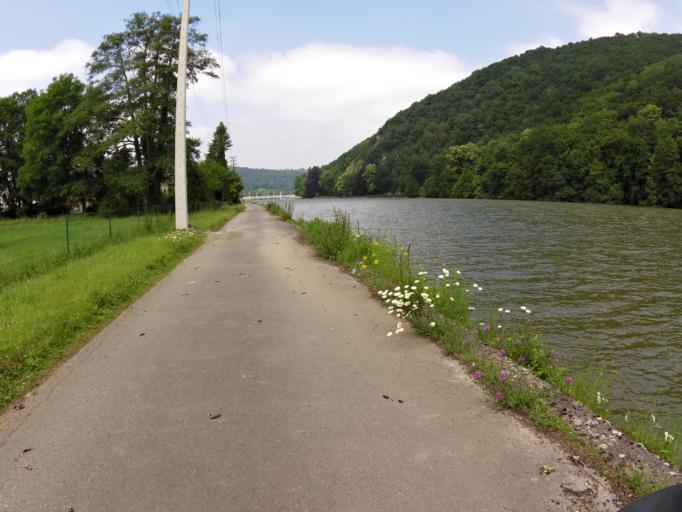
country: BE
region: Wallonia
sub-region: Province de Namur
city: Hastiere-Lavaux
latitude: 50.1937
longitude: 4.8235
